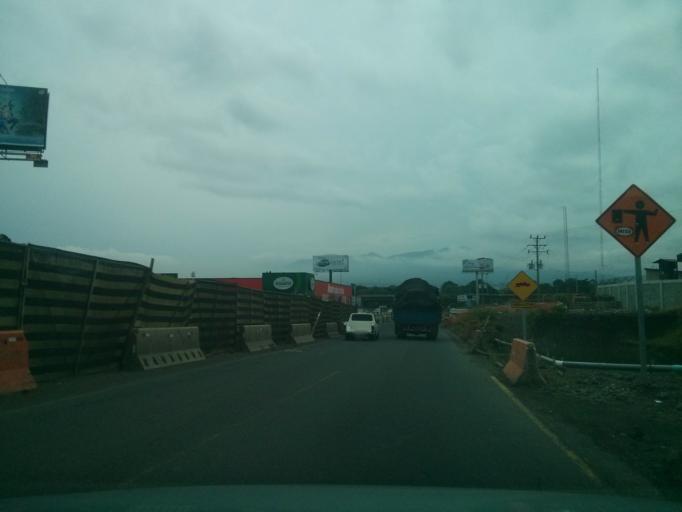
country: CR
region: San Jose
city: San Jose
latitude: 9.9124
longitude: -84.0775
